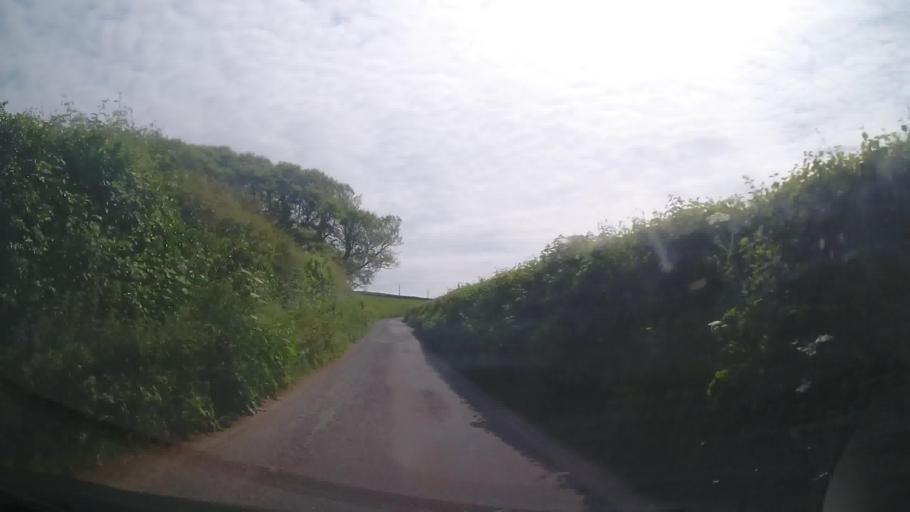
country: GB
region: England
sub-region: Devon
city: Salcombe
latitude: 50.2578
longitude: -3.6775
